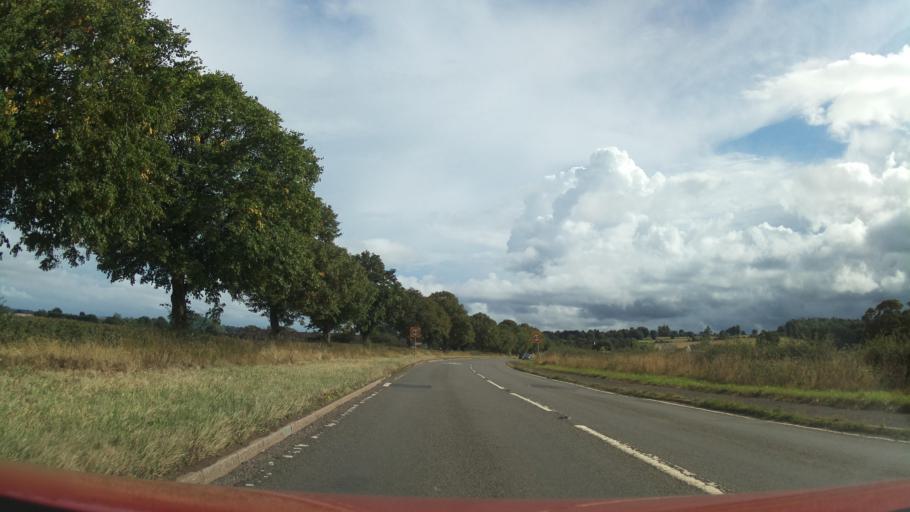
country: GB
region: England
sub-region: Telford and Wrekin
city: Madeley
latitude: 52.6056
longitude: -2.4063
